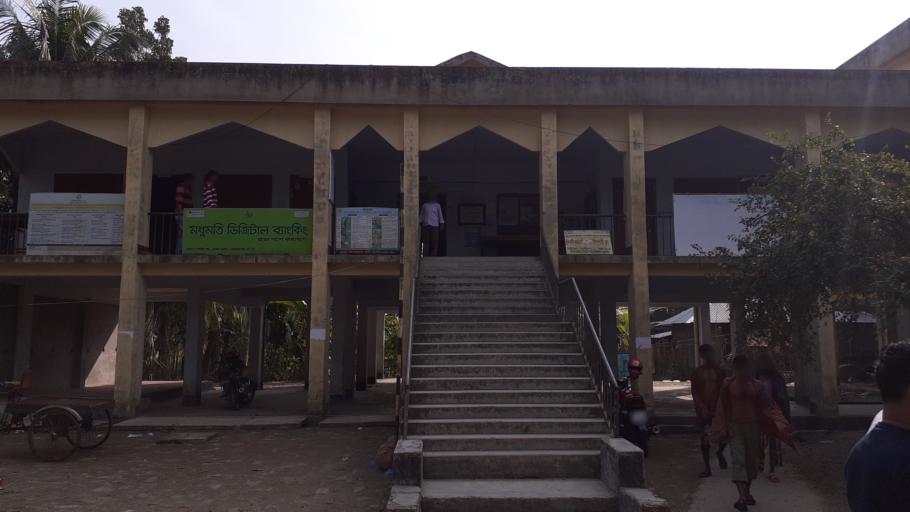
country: BD
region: Khulna
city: Phultala
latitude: 22.5246
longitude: 89.5645
